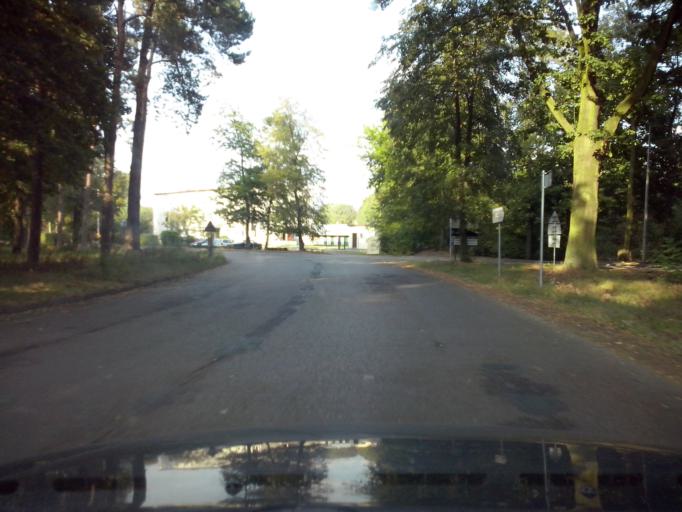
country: PL
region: Subcarpathian Voivodeship
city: Nowa Sarzyna
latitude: 50.3274
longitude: 22.3366
